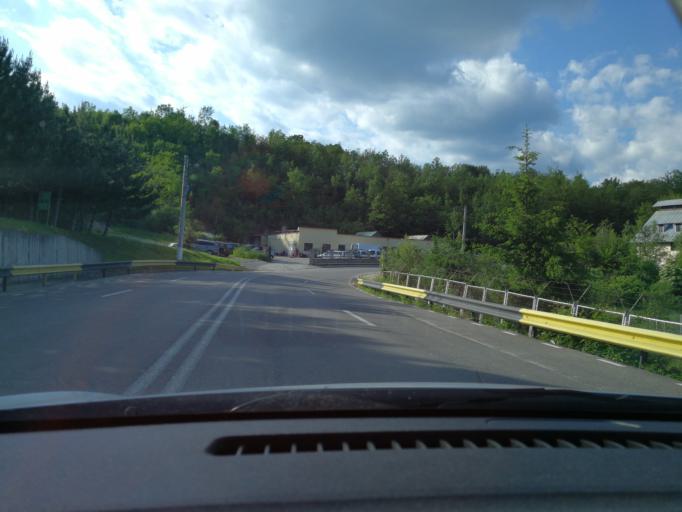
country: RO
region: Prahova
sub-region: Comuna Cornu
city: Cornu de Jos
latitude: 45.1423
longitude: 25.7120
